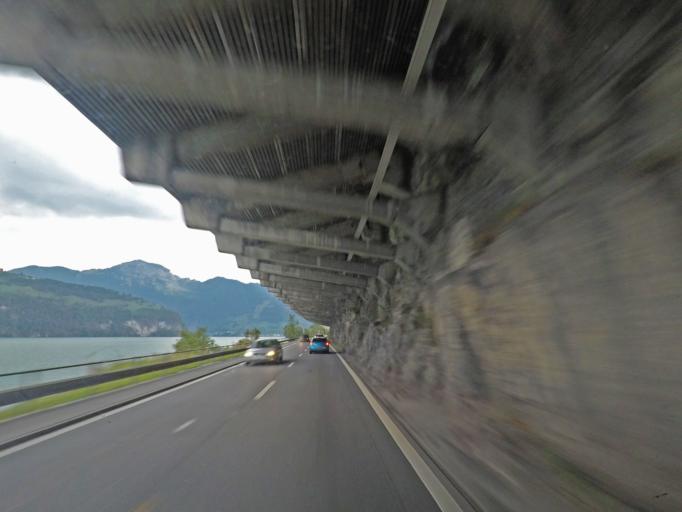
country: CH
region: Schwyz
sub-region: Bezirk Schwyz
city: Ingenbohl
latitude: 46.9647
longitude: 8.6156
